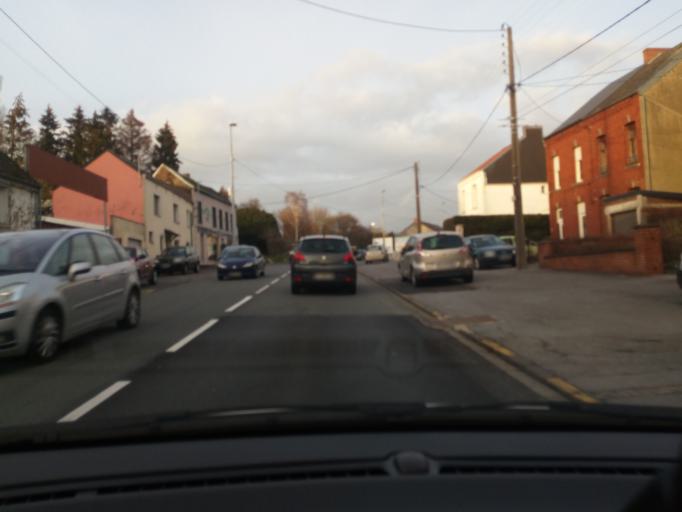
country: FR
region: Nord-Pas-de-Calais
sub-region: Departement du Nord
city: Louvroil
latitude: 50.2599
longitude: 3.9600
